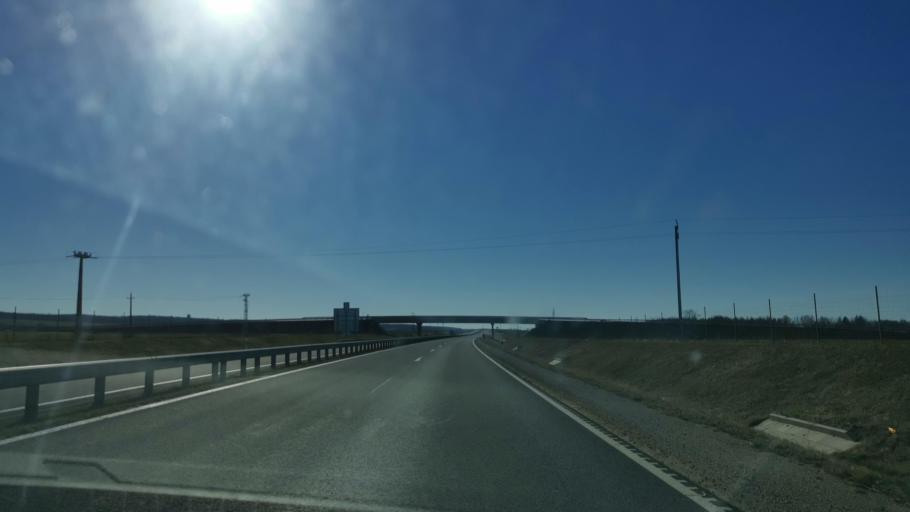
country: HU
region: Somogy
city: Balatonbereny
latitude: 46.6778
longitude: 17.2958
